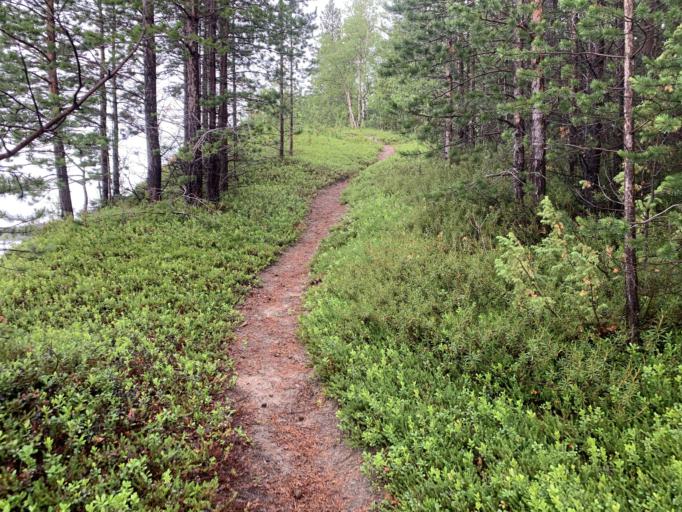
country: RU
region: Murmansk
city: Monchegorsk
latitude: 67.9499
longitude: 33.0217
